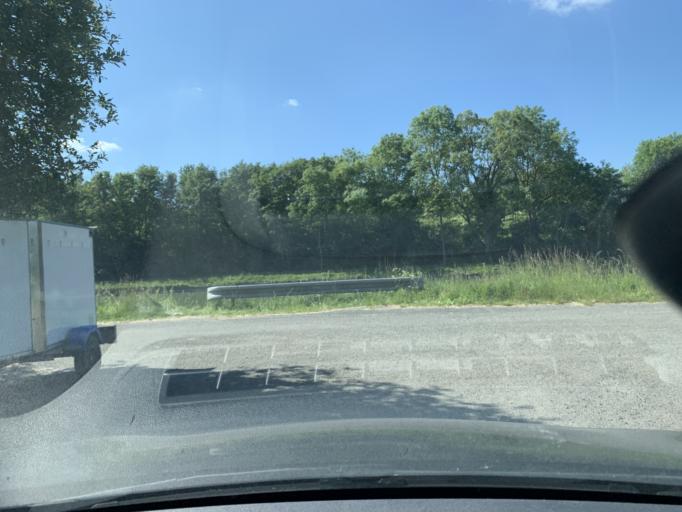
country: FR
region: Nord-Pas-de-Calais
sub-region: Departement du Pas-de-Calais
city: Oisy-le-Verger
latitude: 50.2634
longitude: 3.1384
